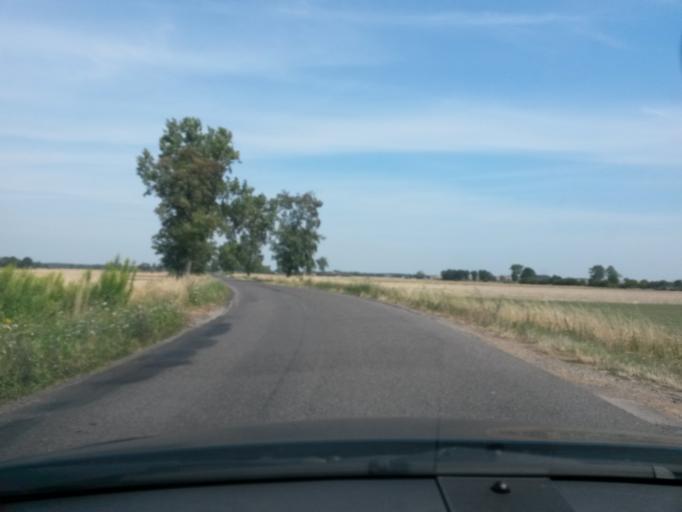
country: PL
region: Lower Silesian Voivodeship
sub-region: Powiat legnicki
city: Prochowice
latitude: 51.1993
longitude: 16.3463
